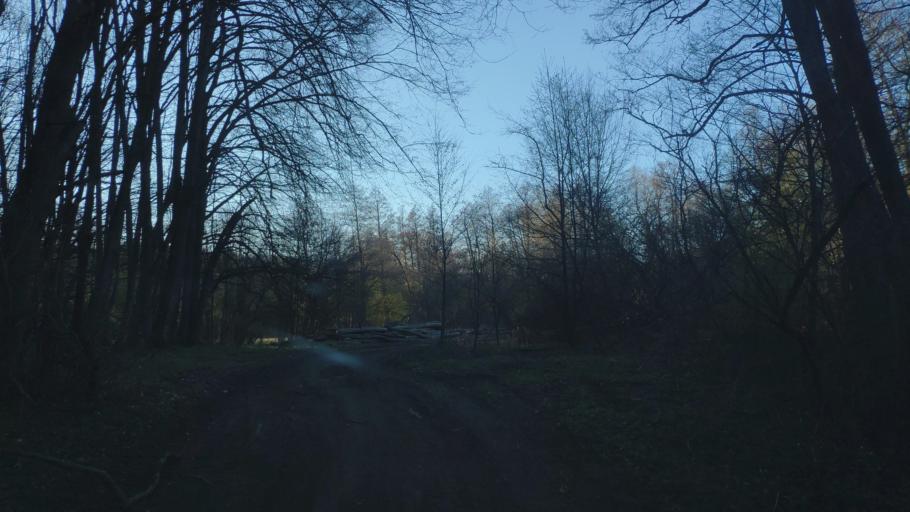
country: HU
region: Borsod-Abauj-Zemplen
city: Putnok
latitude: 48.5203
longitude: 20.3103
